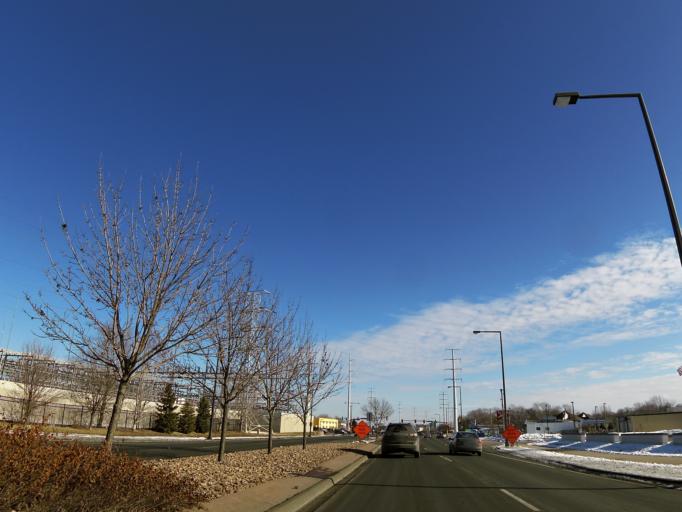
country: US
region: Minnesota
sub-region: Hennepin County
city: Richfield
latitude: 44.8594
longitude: -93.2807
